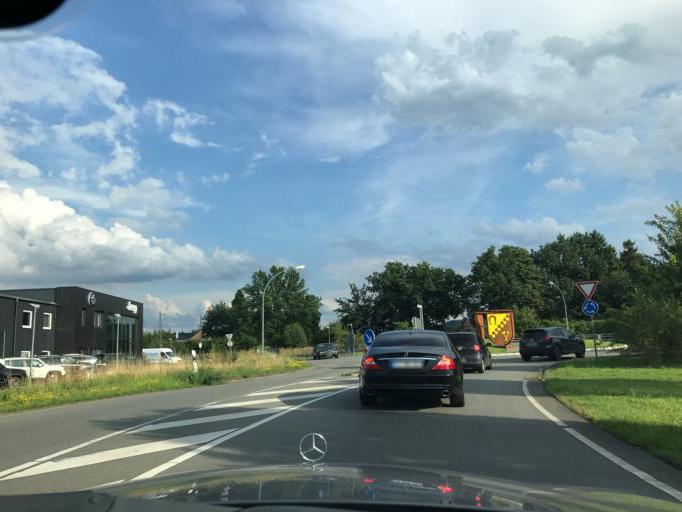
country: DE
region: Lower Saxony
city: Hasbergen
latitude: 52.2432
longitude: 7.9711
